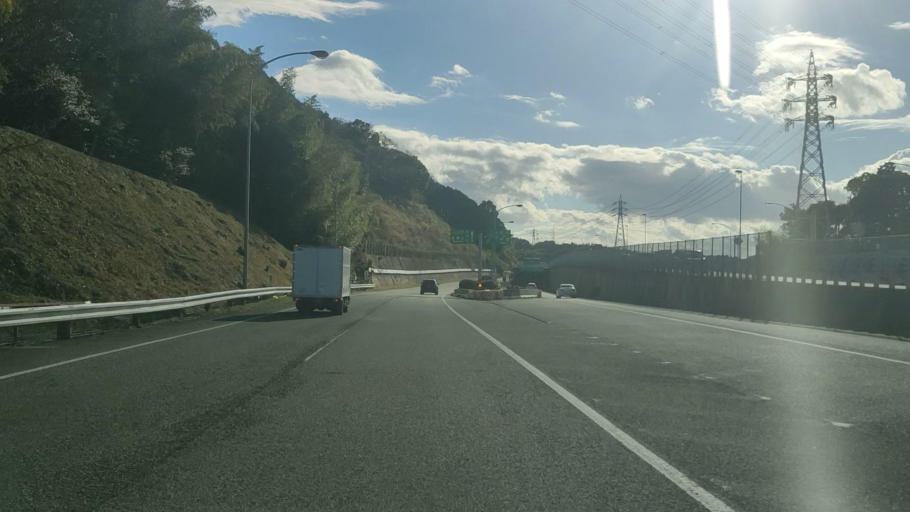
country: JP
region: Fukuoka
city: Kitakyushu
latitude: 33.8465
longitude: 130.7666
